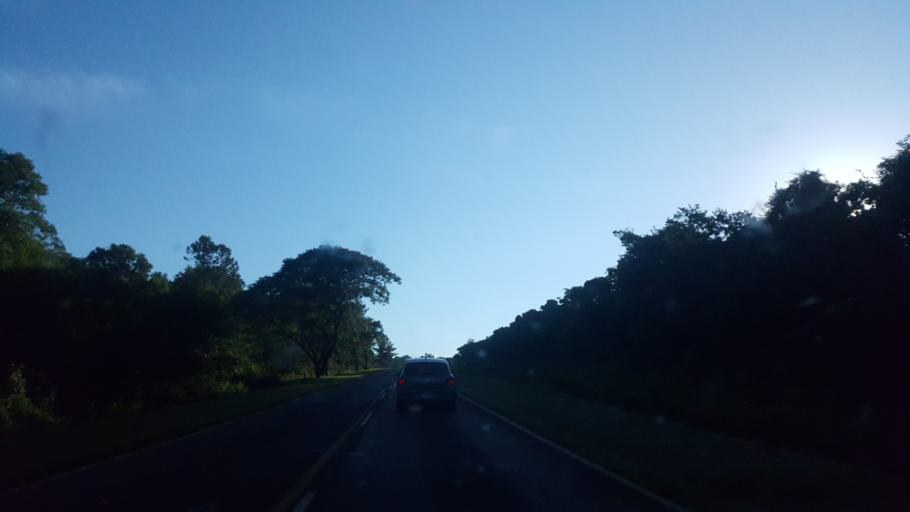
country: AR
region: Misiones
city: El Alcazar
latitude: -26.7198
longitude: -54.8581
